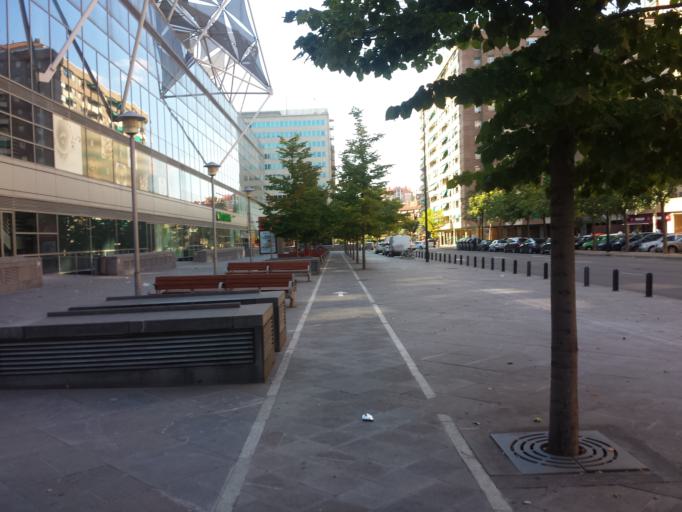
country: ES
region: Aragon
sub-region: Provincia de Zaragoza
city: Delicias
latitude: 41.6400
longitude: -0.9087
